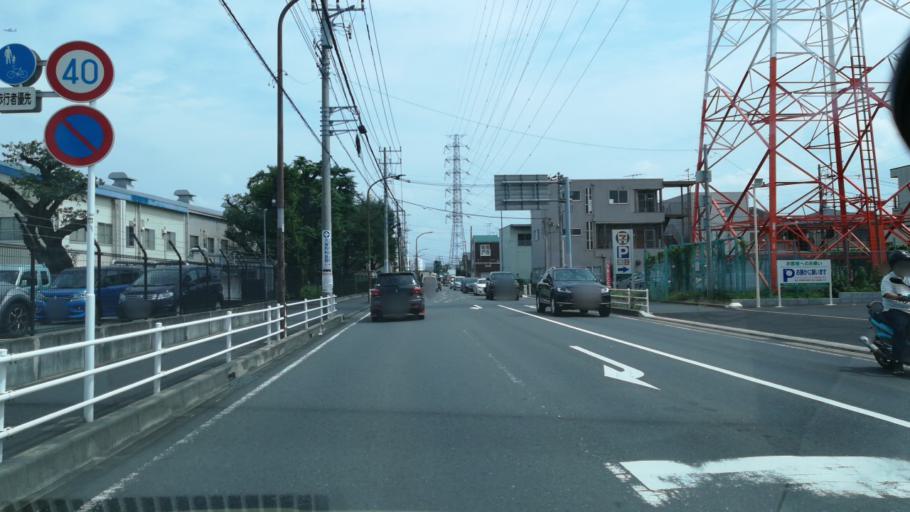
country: JP
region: Tokyo
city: Hachioji
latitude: 35.5872
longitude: 139.3557
